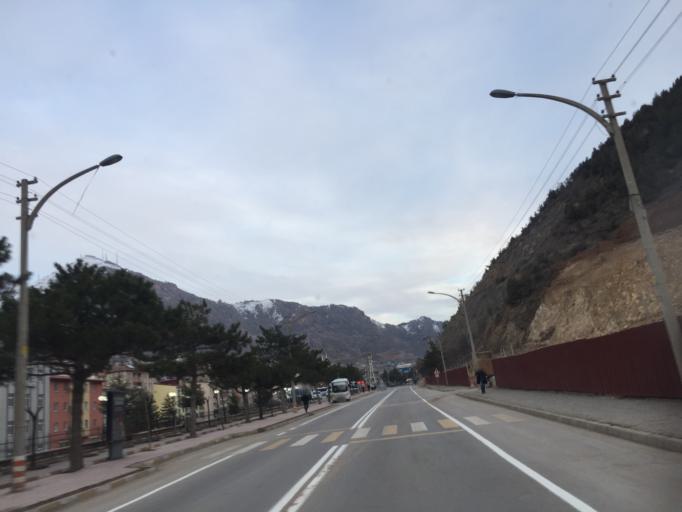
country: TR
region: Gumushane
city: Gumushkhane
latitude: 40.4612
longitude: 39.4698
